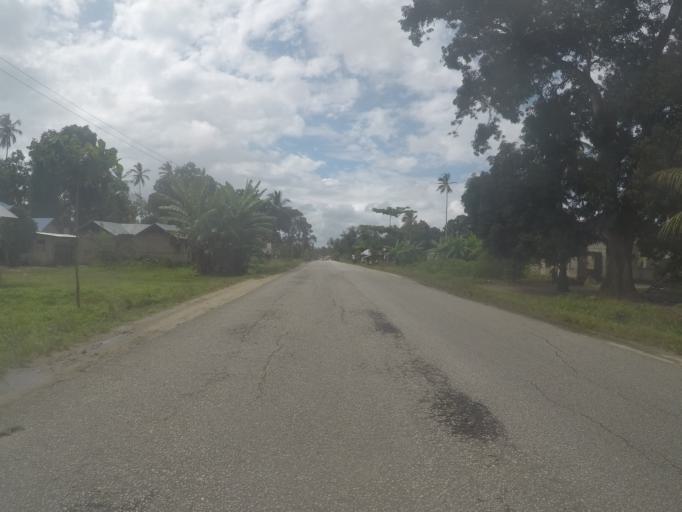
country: TZ
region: Zanzibar North
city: Mkokotoni
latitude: -5.9033
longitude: 39.2516
